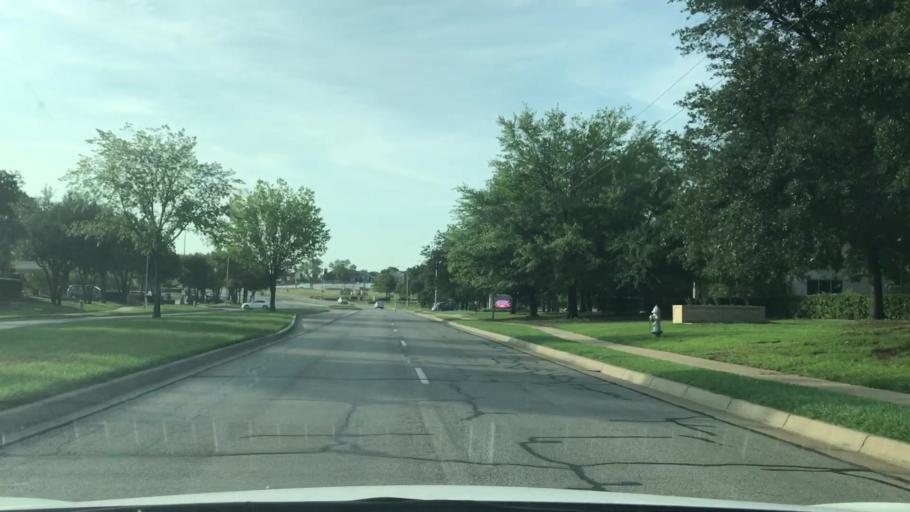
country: US
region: Texas
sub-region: Tarrant County
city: Arlington
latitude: 32.7632
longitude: -97.1202
